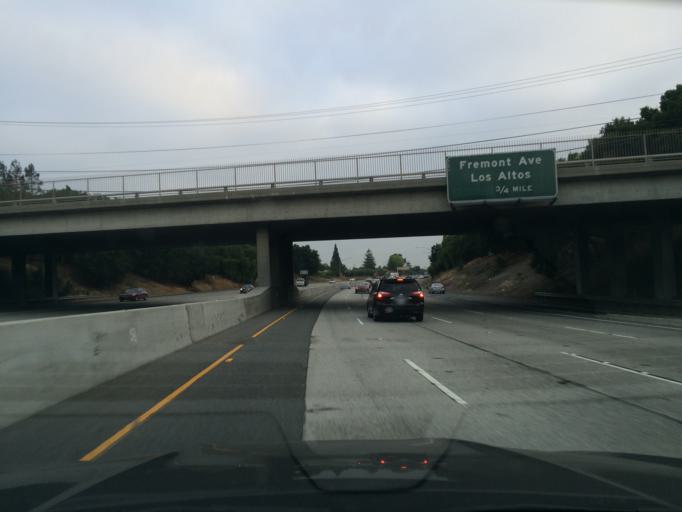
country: US
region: California
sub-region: Santa Clara County
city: Cupertino
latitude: 37.3368
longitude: -122.0593
